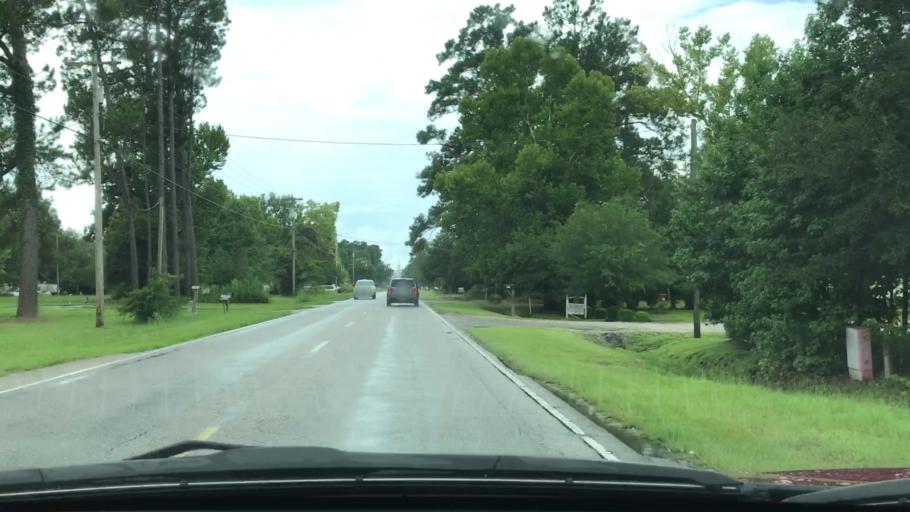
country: US
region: South Carolina
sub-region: Horry County
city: Red Hill
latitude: 33.8512
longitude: -79.0162
